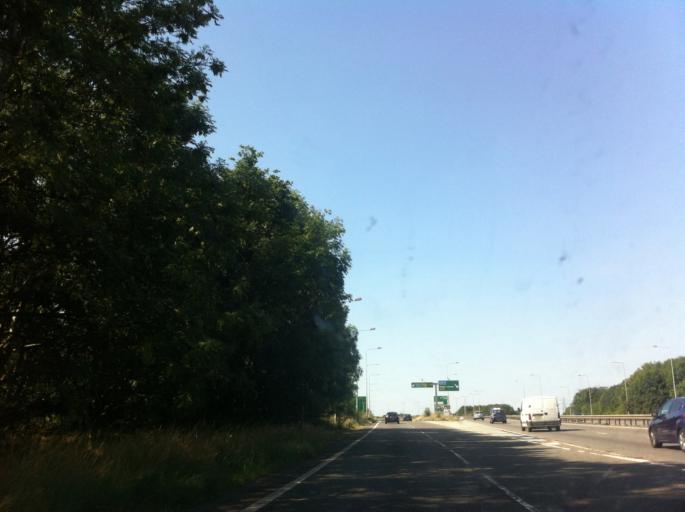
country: GB
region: England
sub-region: Northamptonshire
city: Northampton
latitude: 52.2327
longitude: -0.8629
